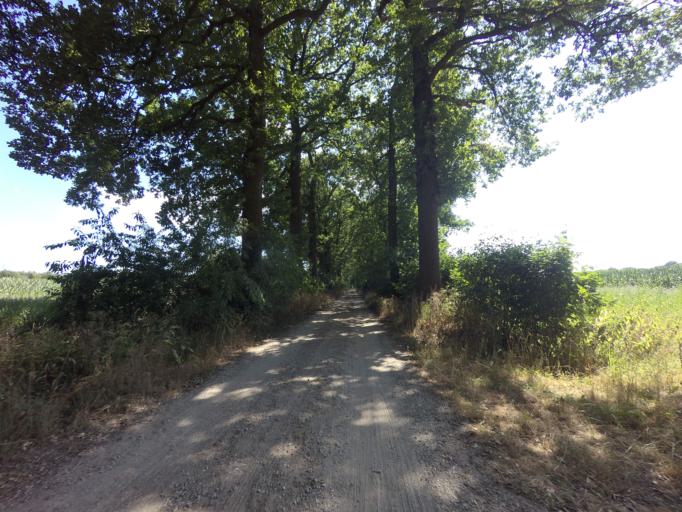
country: NL
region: Utrecht
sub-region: Gemeente De Bilt
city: De Bilt
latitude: 52.1536
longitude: 5.1965
